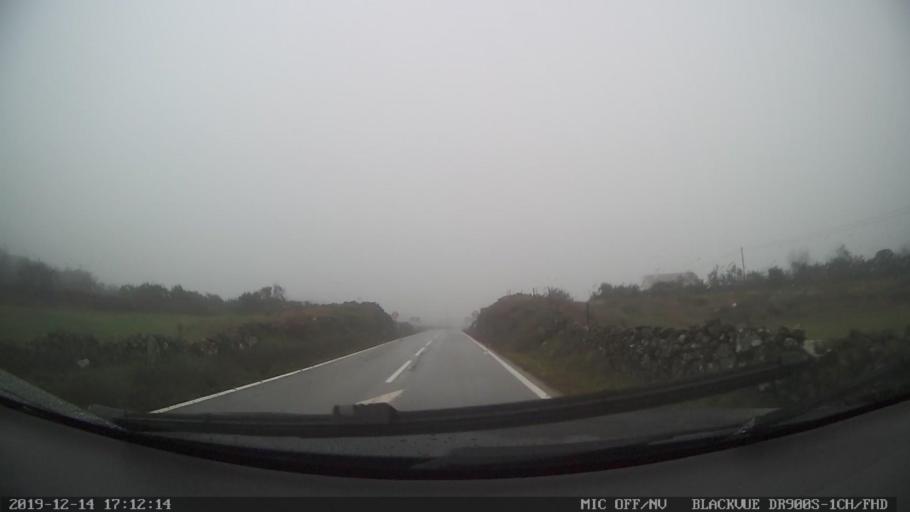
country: PT
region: Vila Real
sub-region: Vila Pouca de Aguiar
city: Vila Pouca de Aguiar
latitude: 41.4918
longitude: -7.6208
